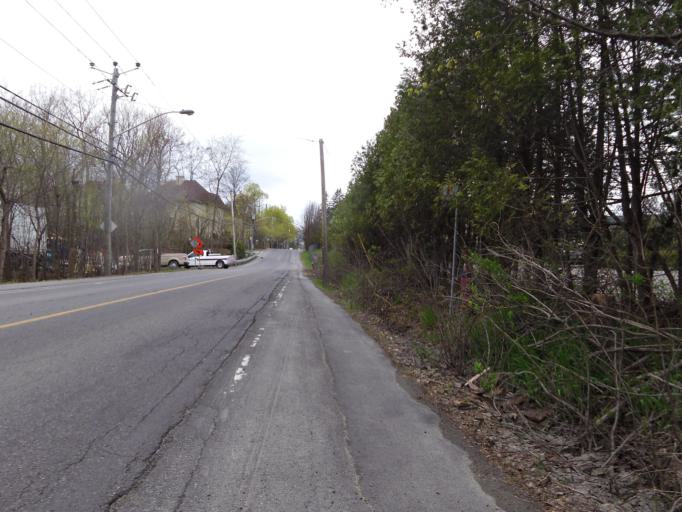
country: CA
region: Quebec
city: Dollard-Des Ormeaux
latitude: 45.5232
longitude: -73.8464
